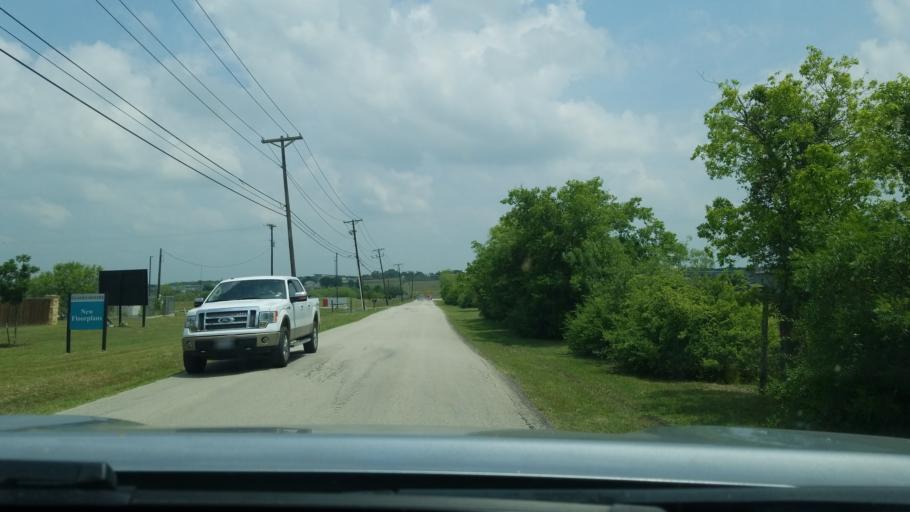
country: US
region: Texas
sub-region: Comal County
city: New Braunfels
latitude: 29.7592
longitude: -98.0668
